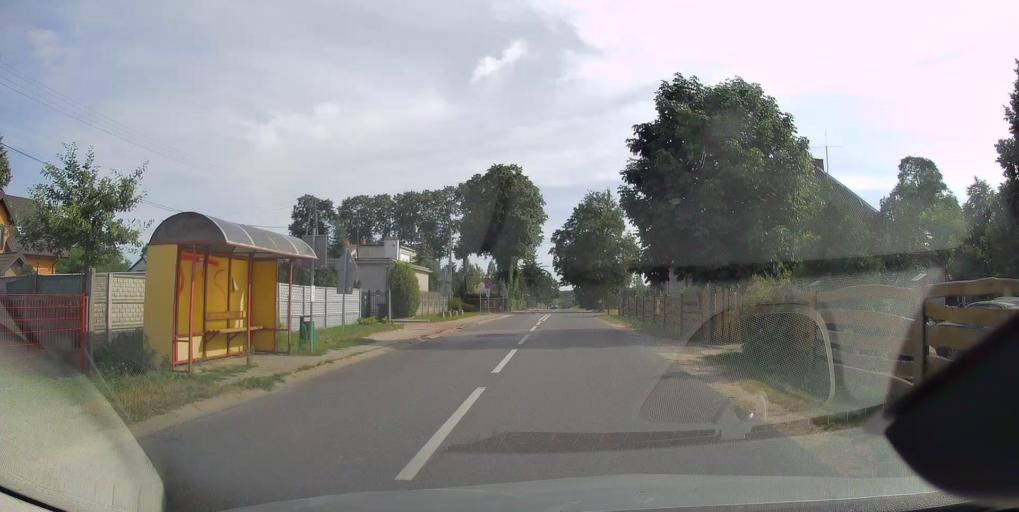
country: PL
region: Lodz Voivodeship
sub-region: Powiat tomaszowski
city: Tomaszow Mazowiecki
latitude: 51.4917
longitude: 19.9887
